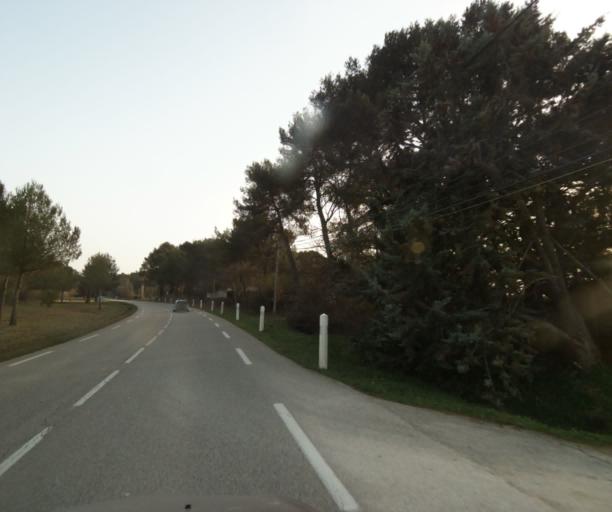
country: FR
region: Provence-Alpes-Cote d'Azur
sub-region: Departement des Bouches-du-Rhone
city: Rognes
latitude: 43.6868
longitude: 5.3409
